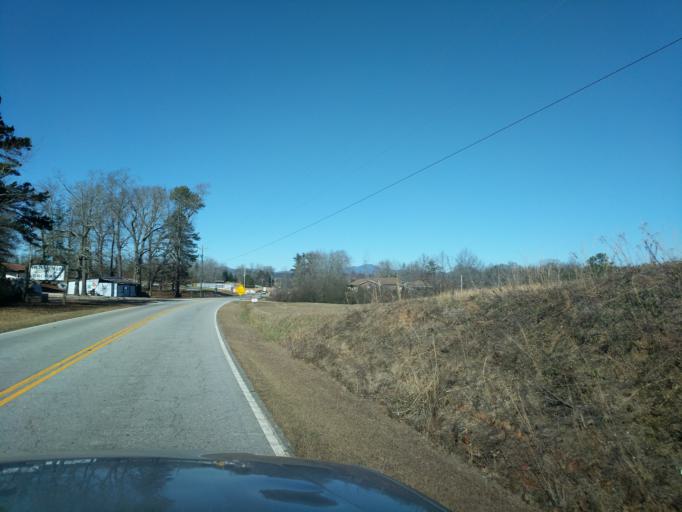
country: US
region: Georgia
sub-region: Rabun County
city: Clayton
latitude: 34.7705
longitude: -83.2570
